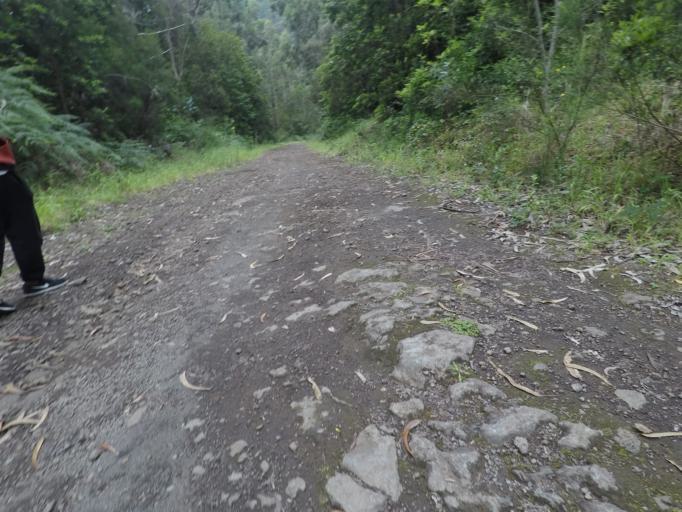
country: PT
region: Madeira
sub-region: Sao Vicente
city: Sao Vicente
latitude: 32.7749
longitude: -17.0488
